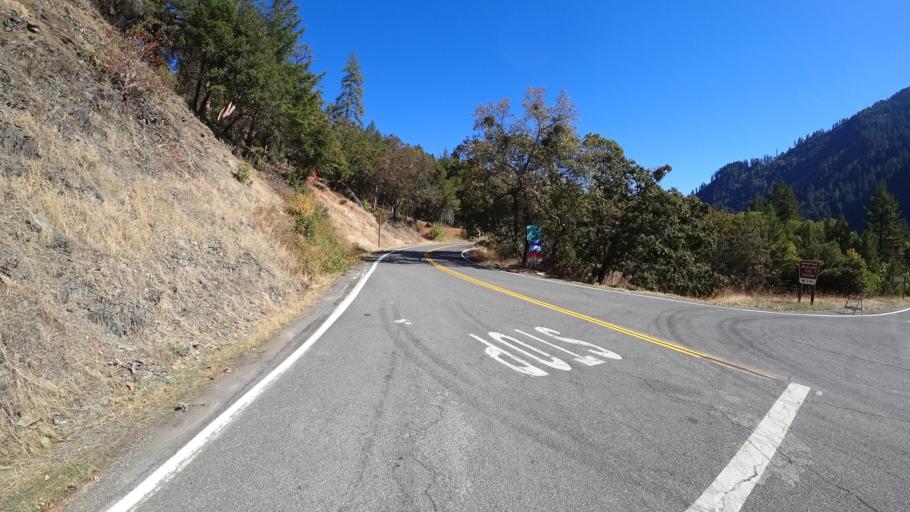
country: US
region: California
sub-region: Siskiyou County
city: Happy Camp
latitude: 41.3810
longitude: -123.4890
